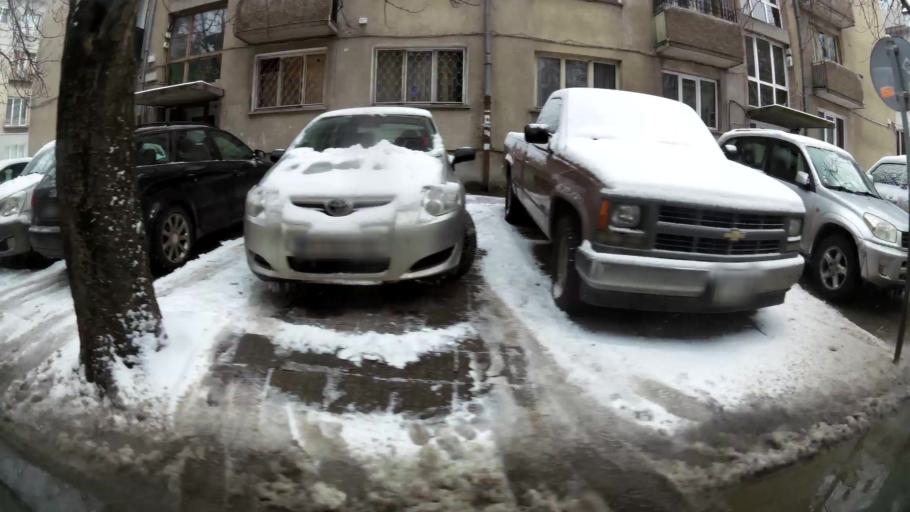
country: BG
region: Sofia-Capital
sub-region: Stolichna Obshtina
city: Sofia
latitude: 42.6924
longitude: 23.3502
